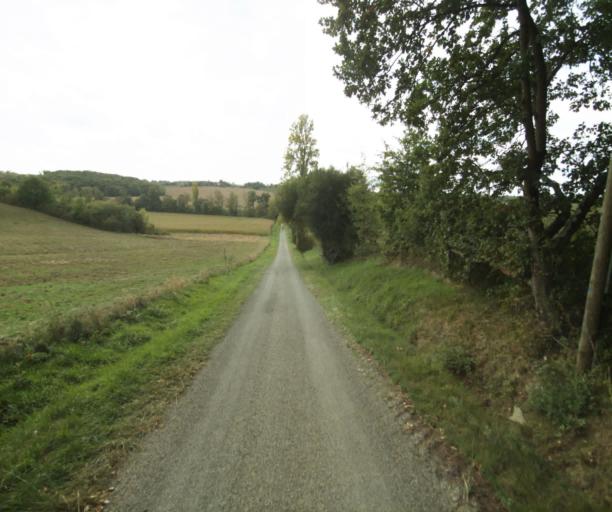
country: FR
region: Midi-Pyrenees
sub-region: Departement du Gers
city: Gondrin
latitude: 43.8397
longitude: 0.1884
